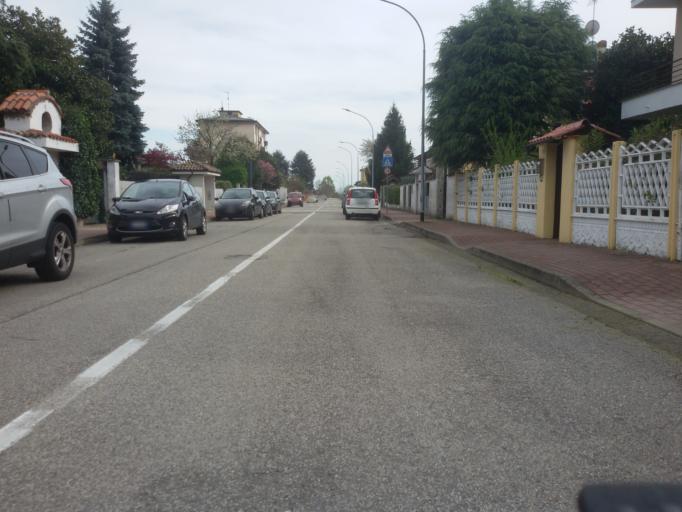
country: IT
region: Lombardy
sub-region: Citta metropolitana di Milano
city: Noviglio
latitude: 45.3600
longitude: 9.0509
